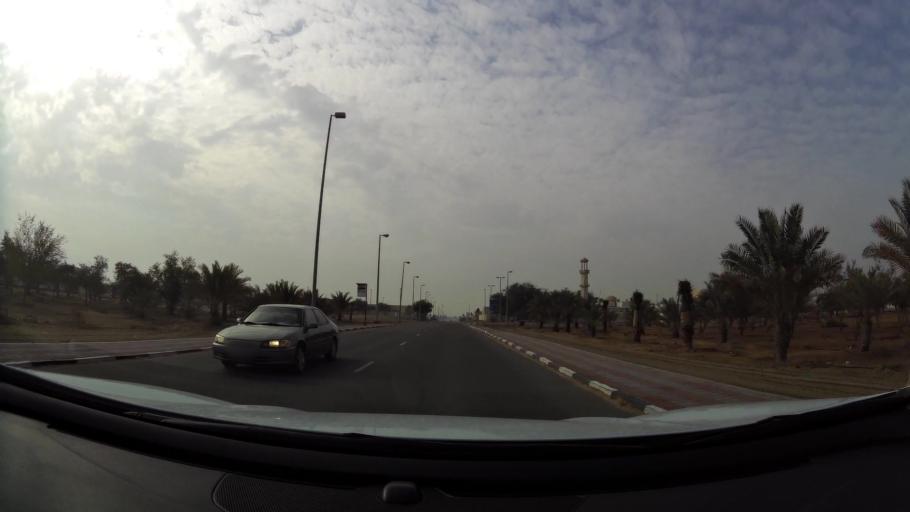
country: AE
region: Abu Dhabi
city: Abu Dhabi
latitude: 24.6820
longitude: 54.7754
